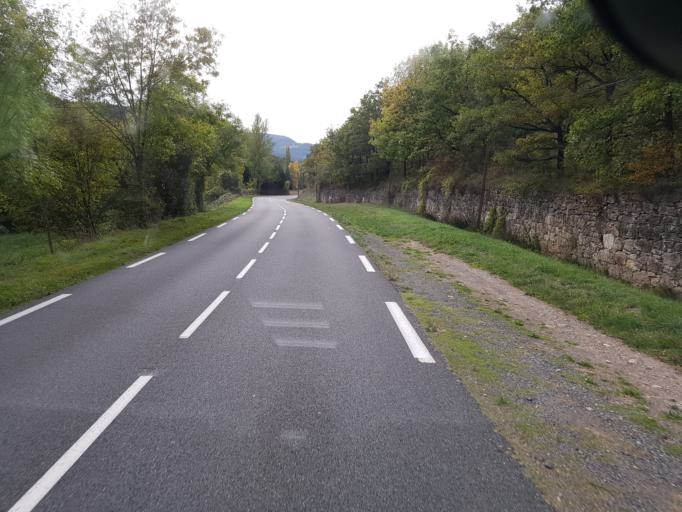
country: FR
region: Midi-Pyrenees
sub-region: Departement de l'Aveyron
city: Saint-Affrique
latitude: 43.9737
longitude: 2.9043
